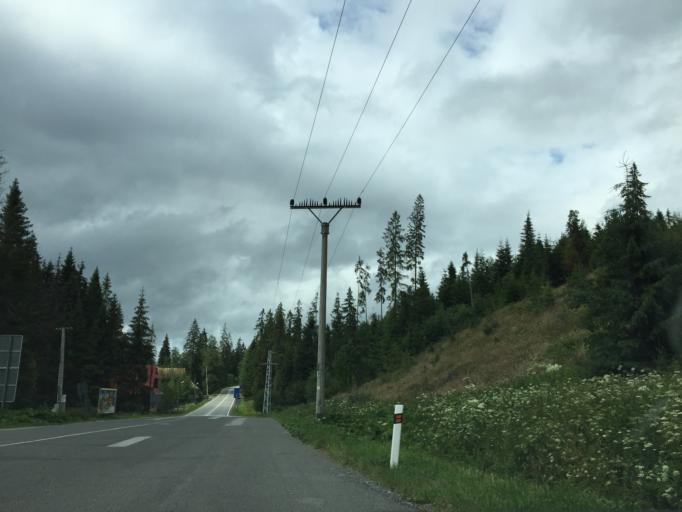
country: PL
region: Lesser Poland Voivodeship
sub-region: Powiat tatrzanski
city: Bukowina Tatrzanska
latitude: 49.3038
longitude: 20.1612
